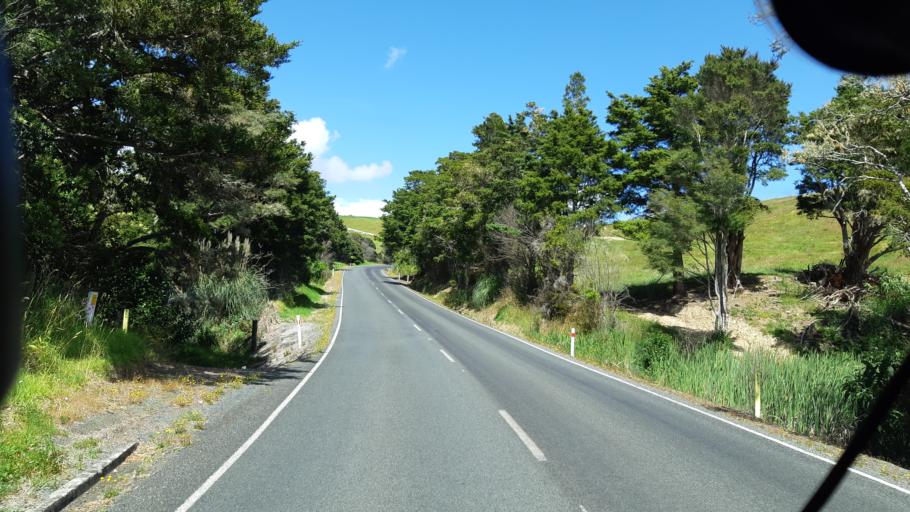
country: NZ
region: Northland
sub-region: Far North District
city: Kaitaia
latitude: -35.2703
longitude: 173.4861
